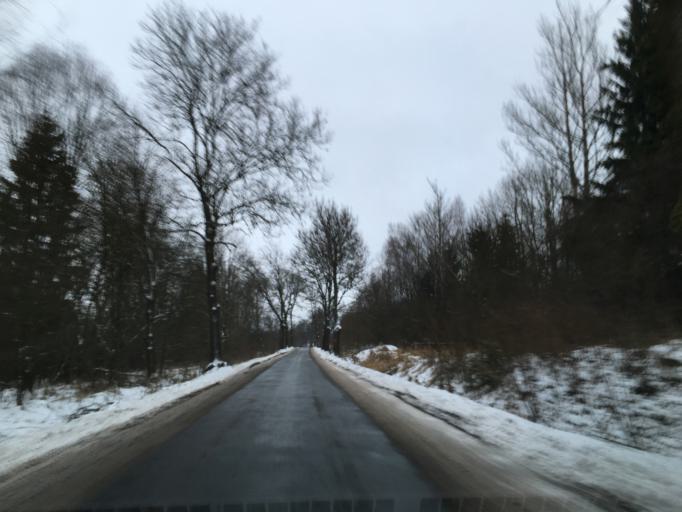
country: CZ
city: Radvanice
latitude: 50.6412
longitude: 16.0472
